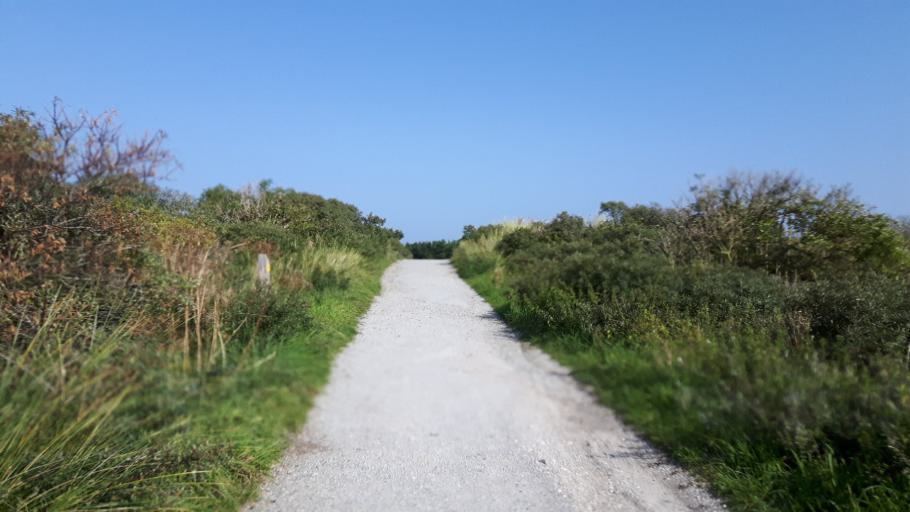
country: NL
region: Friesland
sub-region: Gemeente Ameland
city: Nes
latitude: 53.4573
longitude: 5.8147
